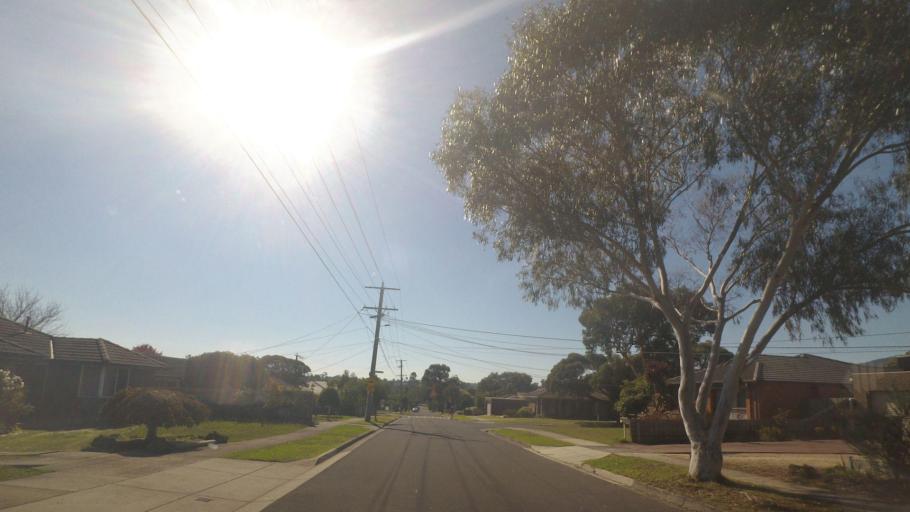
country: AU
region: Victoria
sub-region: Knox
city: Boronia
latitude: -37.8725
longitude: 145.2759
